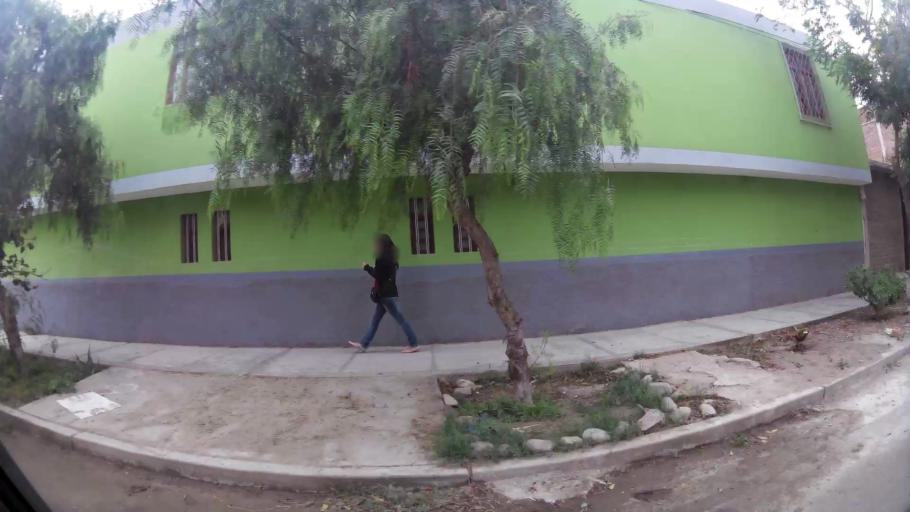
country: PE
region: La Libertad
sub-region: Provincia de Trujillo
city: Buenos Aires
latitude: -8.1417
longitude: -79.0466
